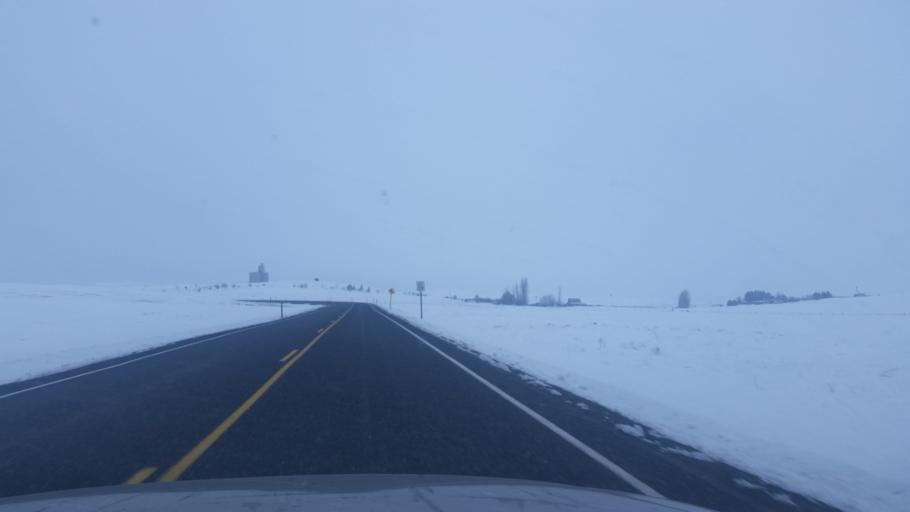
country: US
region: Washington
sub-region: Spokane County
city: Medical Lake
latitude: 47.5470
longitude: -117.8461
